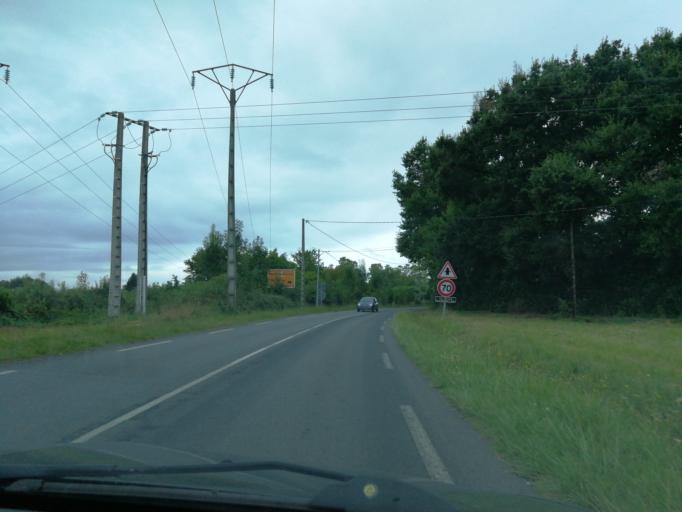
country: FR
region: Midi-Pyrenees
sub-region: Departement des Hautes-Pyrenees
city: Bazet
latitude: 43.2686
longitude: 0.0784
